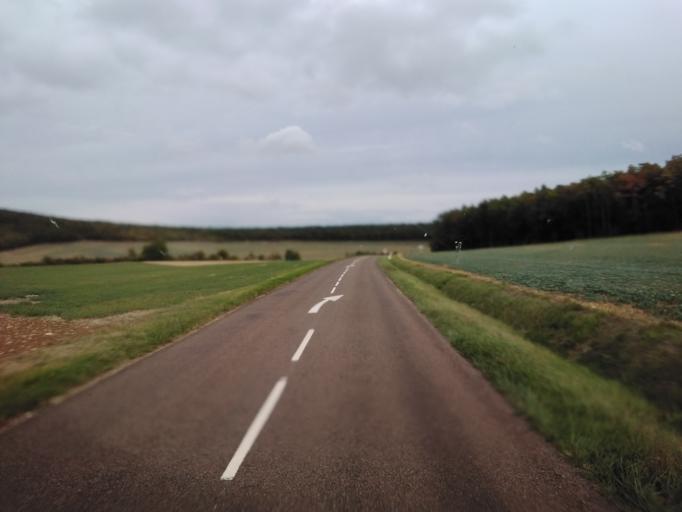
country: FR
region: Champagne-Ardenne
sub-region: Departement de l'Aube
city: Les Riceys
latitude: 47.9583
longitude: 4.3653
